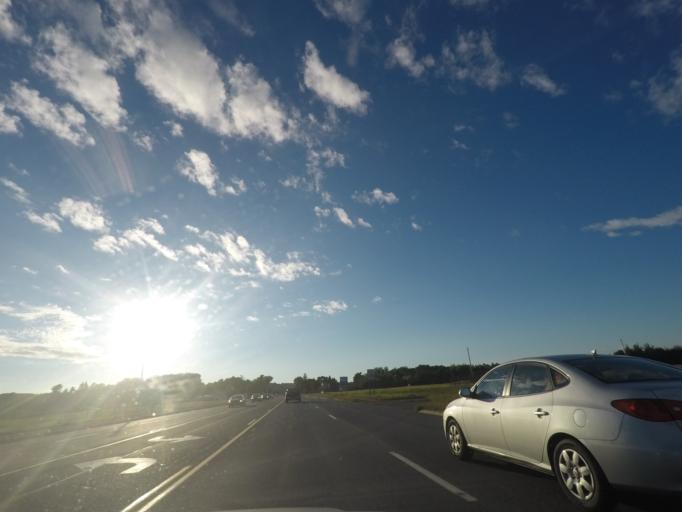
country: US
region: New York
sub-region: Schenectady County
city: Niskayuna
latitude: 42.7644
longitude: -73.8047
